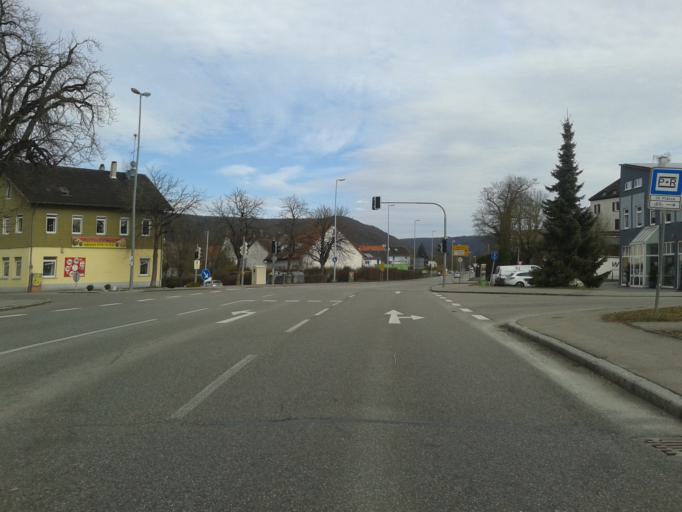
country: DE
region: Baden-Wuerttemberg
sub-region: Tuebingen Region
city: Schelklingen
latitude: 48.3721
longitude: 9.7344
